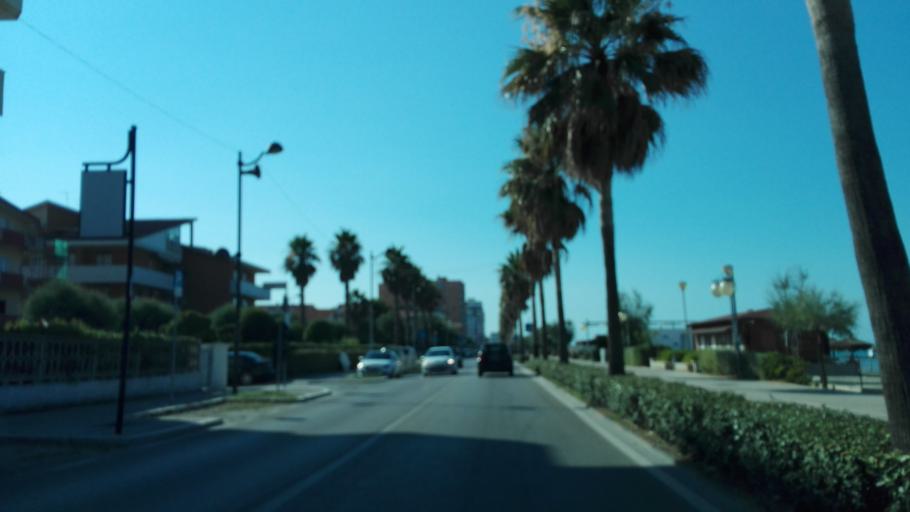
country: IT
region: Abruzzo
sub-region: Provincia di Pescara
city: Montesilvano Marina
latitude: 42.5128
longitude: 14.1662
